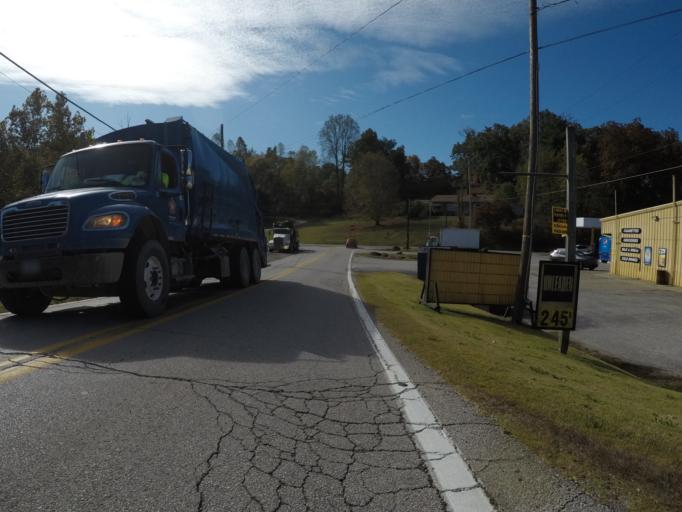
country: US
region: Ohio
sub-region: Lawrence County
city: Burlington
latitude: 38.3573
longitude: -82.5243
